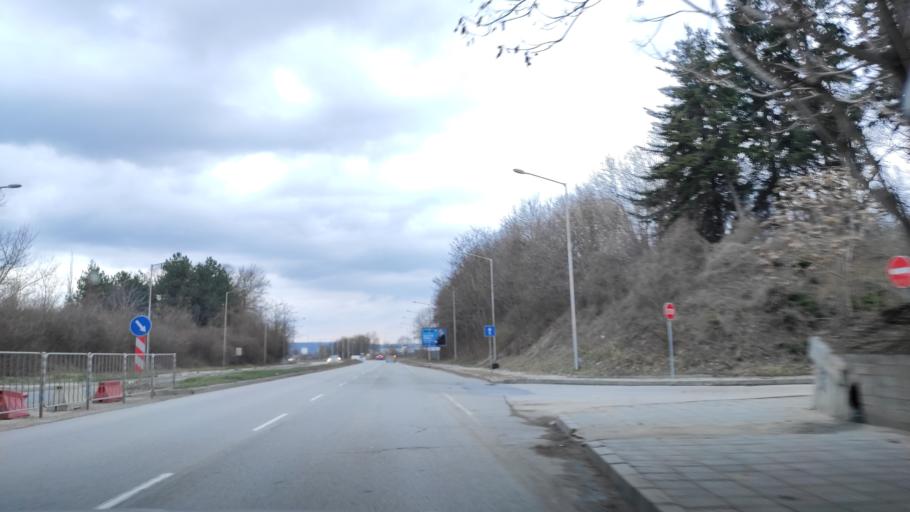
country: BG
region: Varna
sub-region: Obshtina Aksakovo
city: Aksakovo
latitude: 43.2279
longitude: 27.8604
